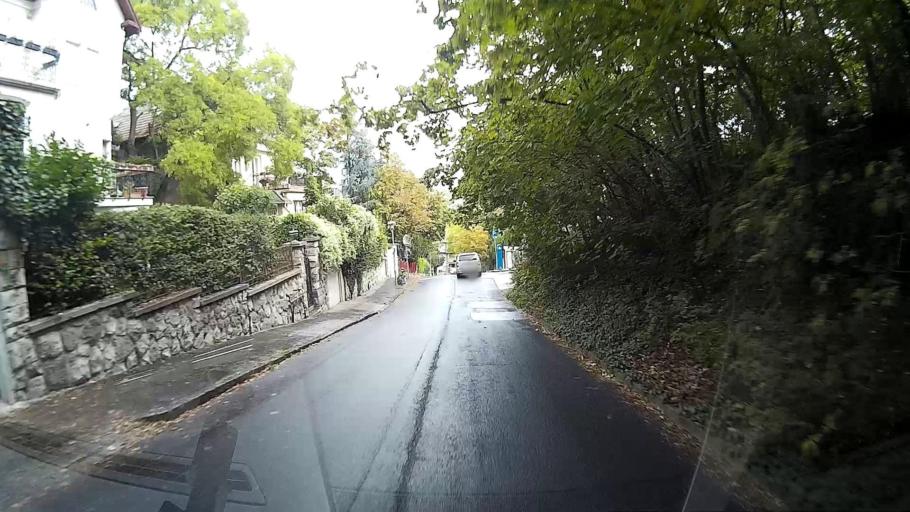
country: HU
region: Budapest
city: Budapest XII. keruelet
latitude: 47.5045
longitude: 19.0124
